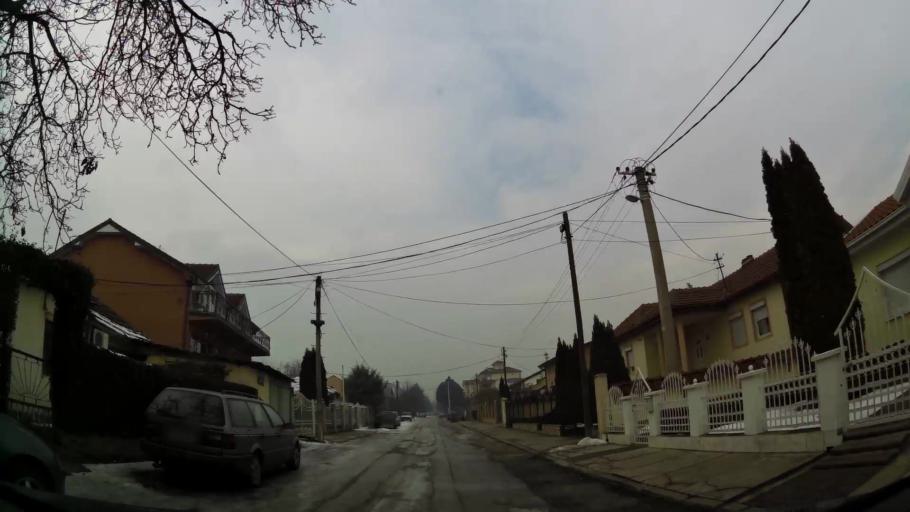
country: MK
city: Creshevo
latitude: 42.0008
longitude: 21.4929
